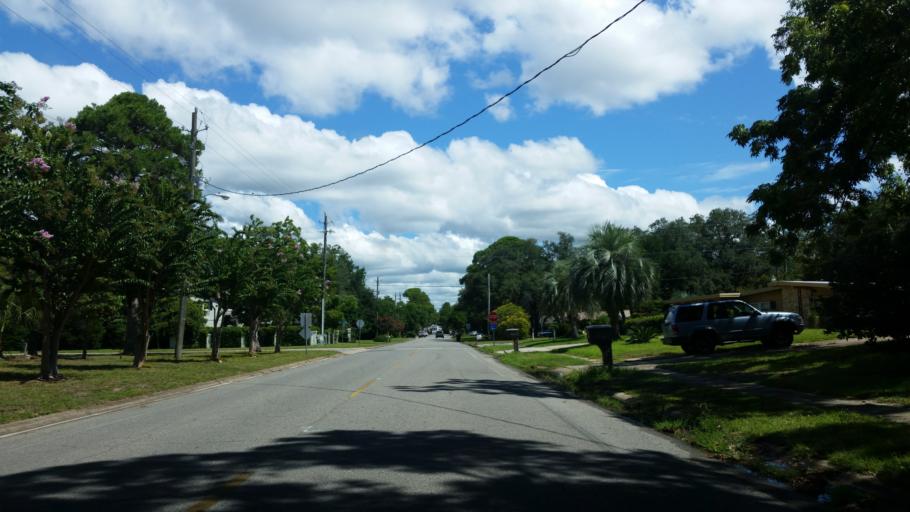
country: US
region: Florida
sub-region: Okaloosa County
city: Ocean City
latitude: 30.4232
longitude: -86.5932
